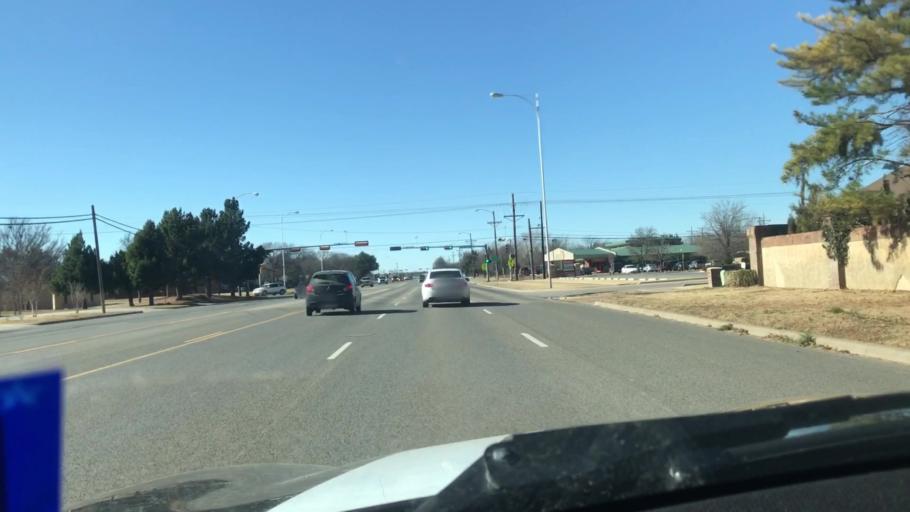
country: US
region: Texas
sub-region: Lubbock County
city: Lubbock
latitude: 33.5779
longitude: -101.9299
